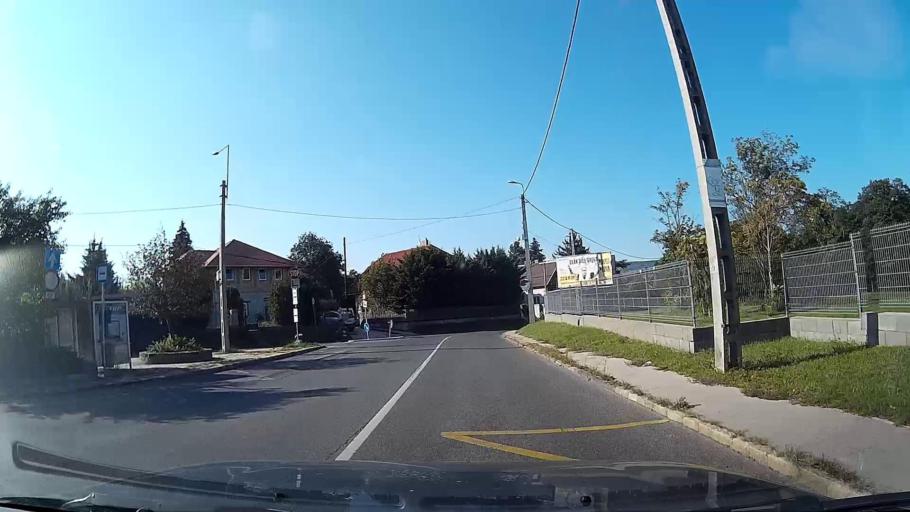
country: HU
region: Pest
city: Budaors
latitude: 47.4359
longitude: 18.9789
